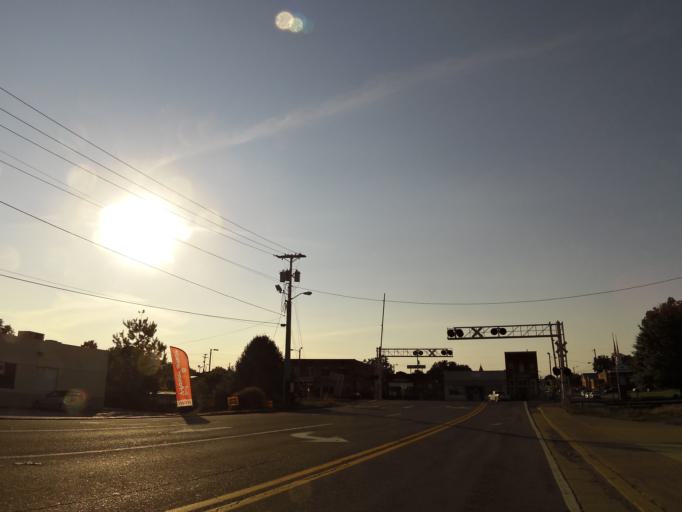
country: US
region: Tennessee
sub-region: McMinn County
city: Englewood
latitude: 35.4253
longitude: -84.4859
